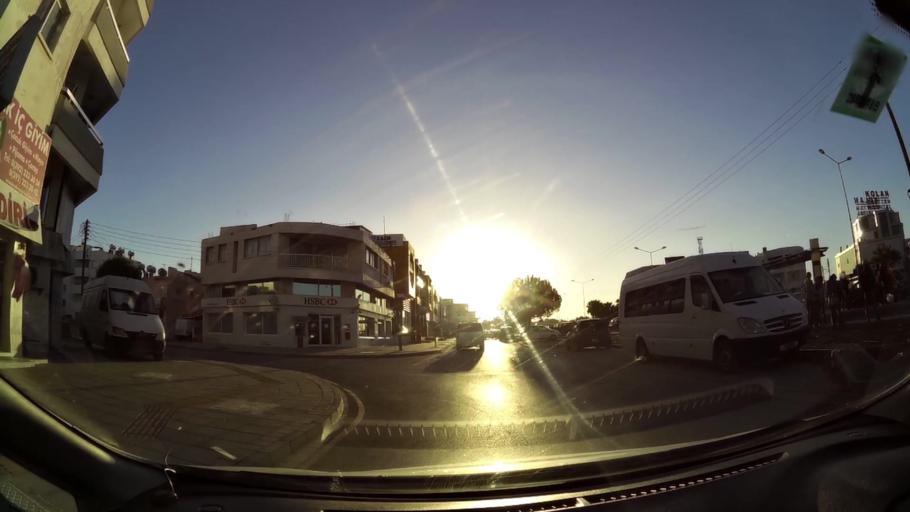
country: CY
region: Lefkosia
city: Nicosia
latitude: 35.2082
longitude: 33.3178
